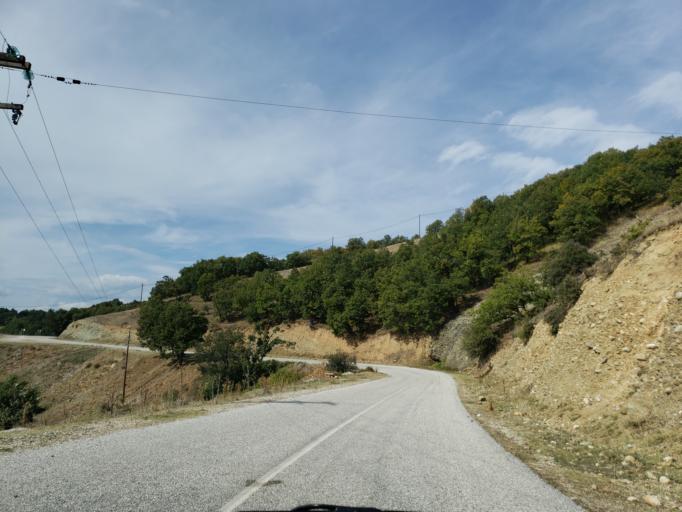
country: GR
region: Thessaly
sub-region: Trikala
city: Kastraki
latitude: 39.7687
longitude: 21.6649
